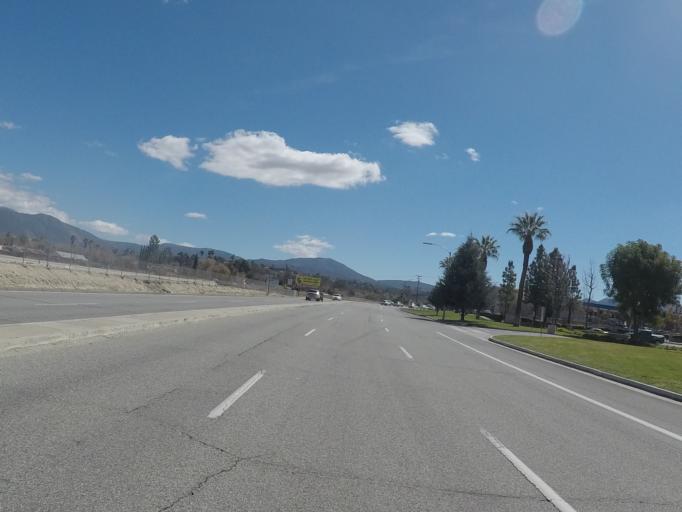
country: US
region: California
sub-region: Riverside County
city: Valle Vista
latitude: 33.7494
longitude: -116.9023
